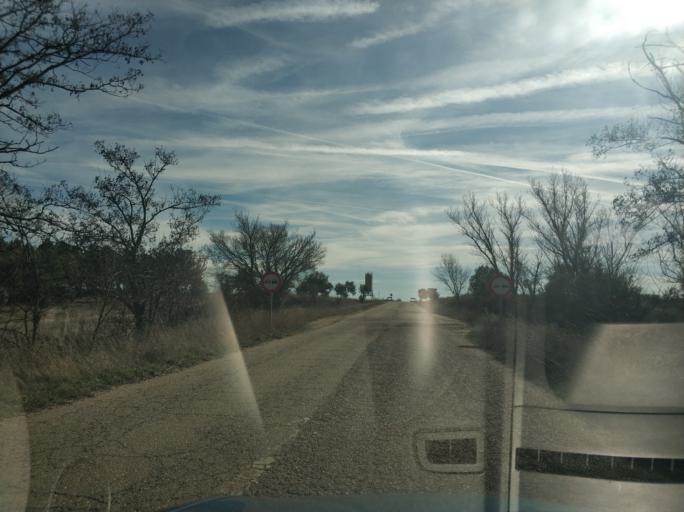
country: ES
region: Castille and Leon
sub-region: Provincia de Zamora
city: Cuelgamures
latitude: 41.2483
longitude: -5.7083
